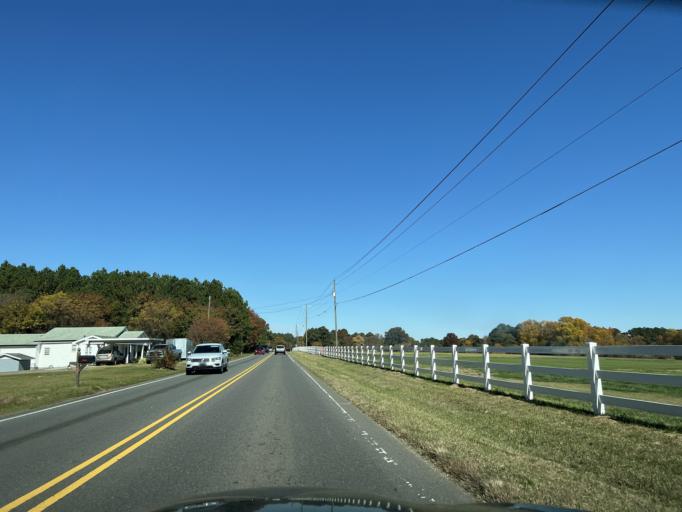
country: US
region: North Carolina
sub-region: Wake County
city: West Raleigh
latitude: 35.7387
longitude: -78.6814
